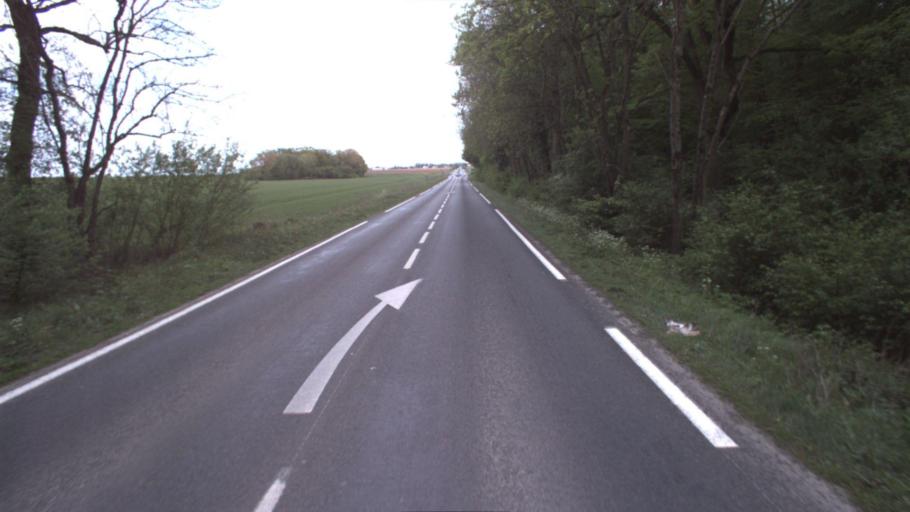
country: FR
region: Ile-de-France
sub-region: Departement de Seine-et-Marne
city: Saint-Pathus
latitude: 49.0563
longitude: 2.7830
